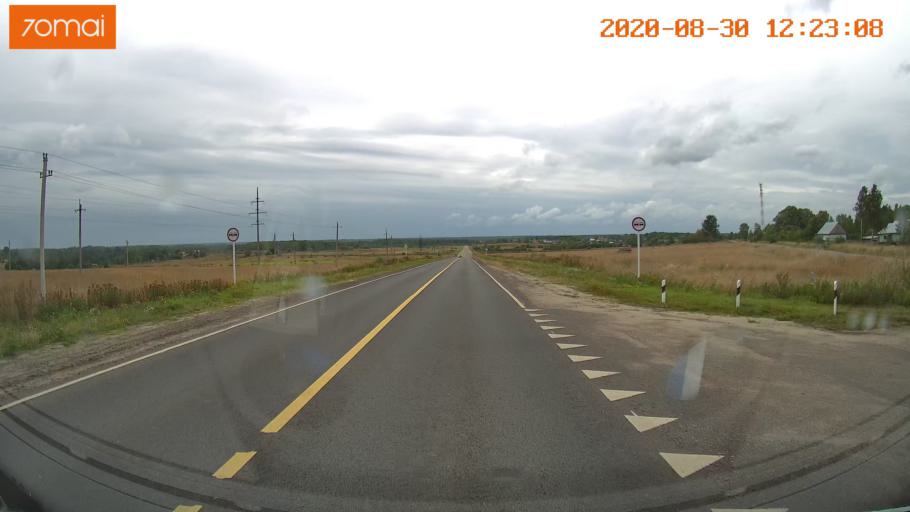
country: RU
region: Ivanovo
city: Yur'yevets
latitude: 57.3314
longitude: 42.8322
